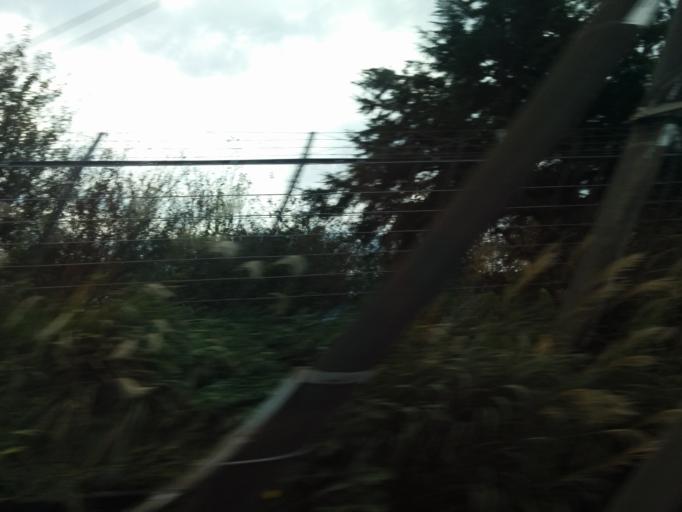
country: JP
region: Shizuoka
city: Numazu
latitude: 35.1252
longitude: 138.8535
